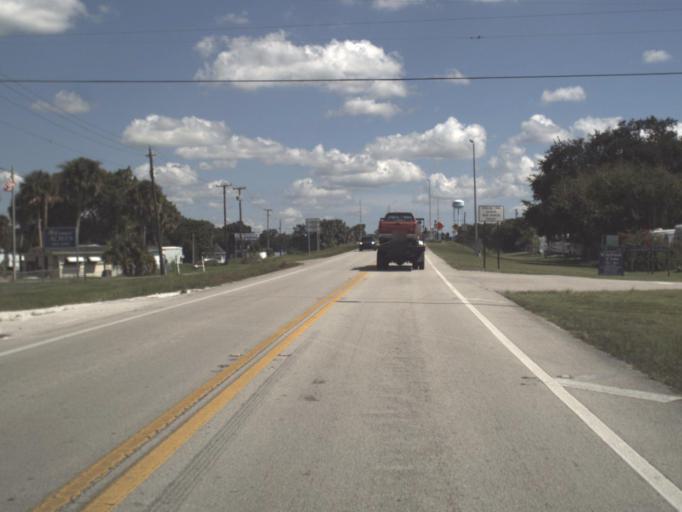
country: US
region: Florida
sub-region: Okeechobee County
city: Taylor Creek
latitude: 27.2097
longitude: -80.8009
